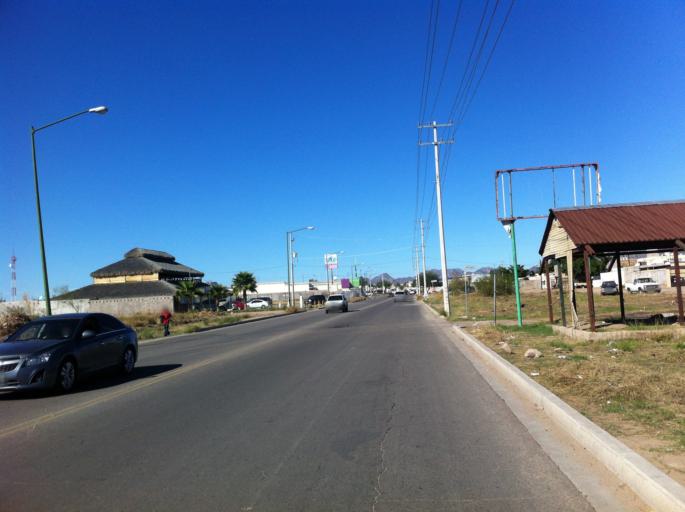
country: MX
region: Sonora
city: Hermosillo
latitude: 29.1132
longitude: -111.0055
